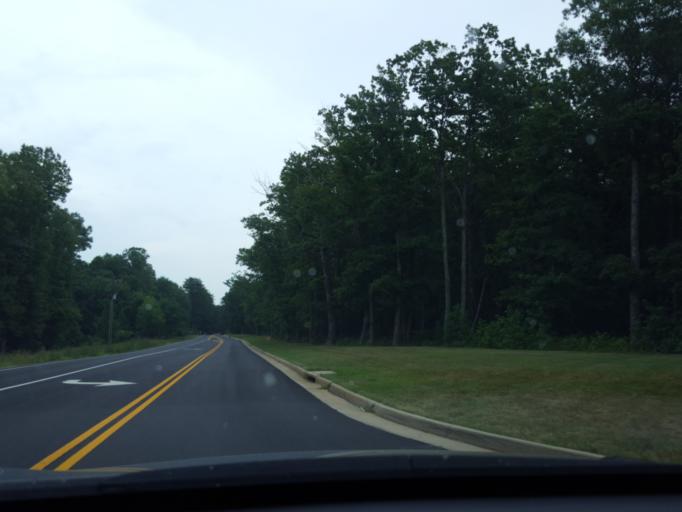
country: US
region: Virginia
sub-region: Spotsylvania County
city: Spotsylvania
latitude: 38.2814
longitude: -77.7360
